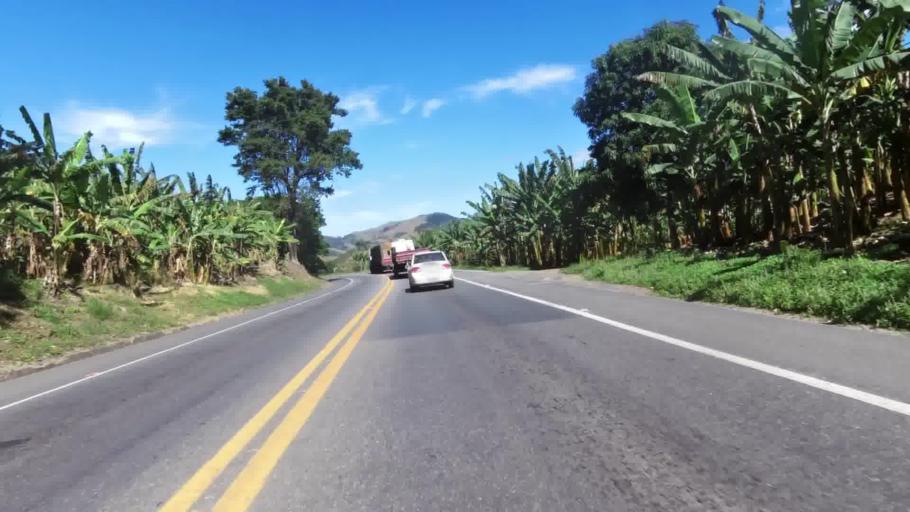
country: BR
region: Espirito Santo
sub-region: Iconha
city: Iconha
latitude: -20.7975
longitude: -40.8223
